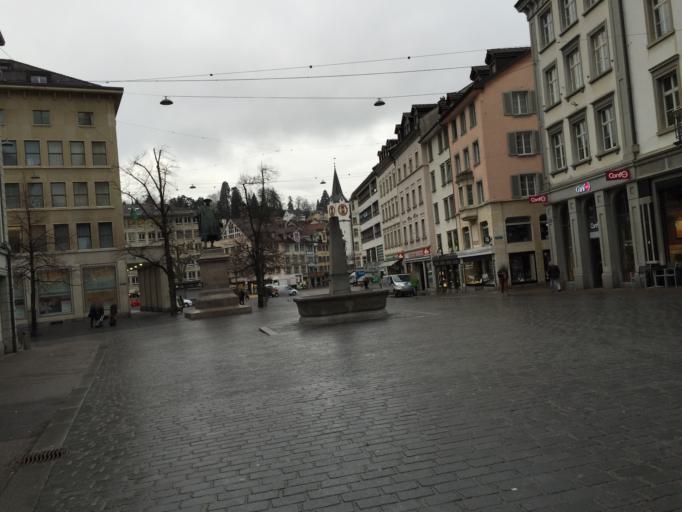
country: CH
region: Saint Gallen
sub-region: Wahlkreis St. Gallen
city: Sankt Gallen
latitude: 47.4254
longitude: 9.3765
